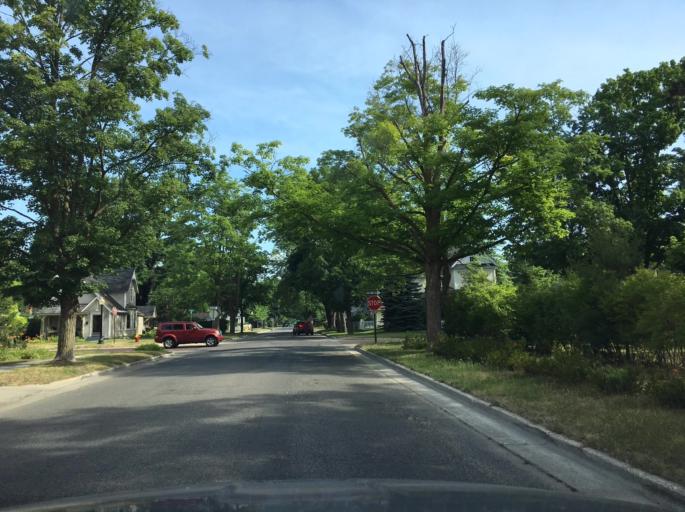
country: US
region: Michigan
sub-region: Grand Traverse County
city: Traverse City
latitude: 44.7589
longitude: -85.6329
